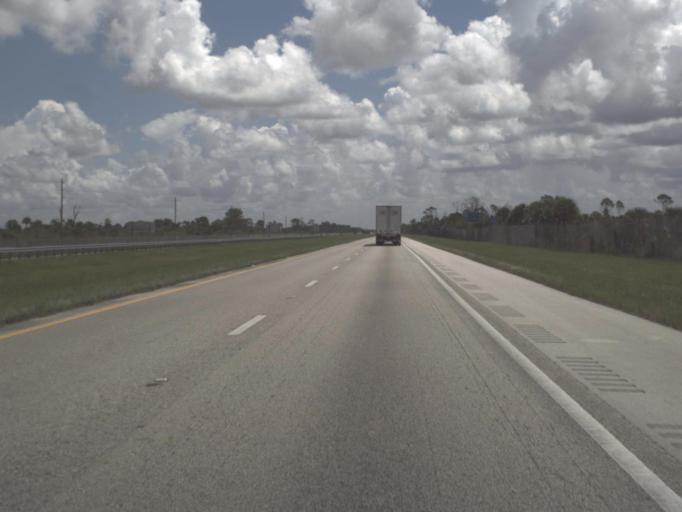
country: US
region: Florida
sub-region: Collier County
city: Immokalee
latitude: 26.1547
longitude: -81.3308
